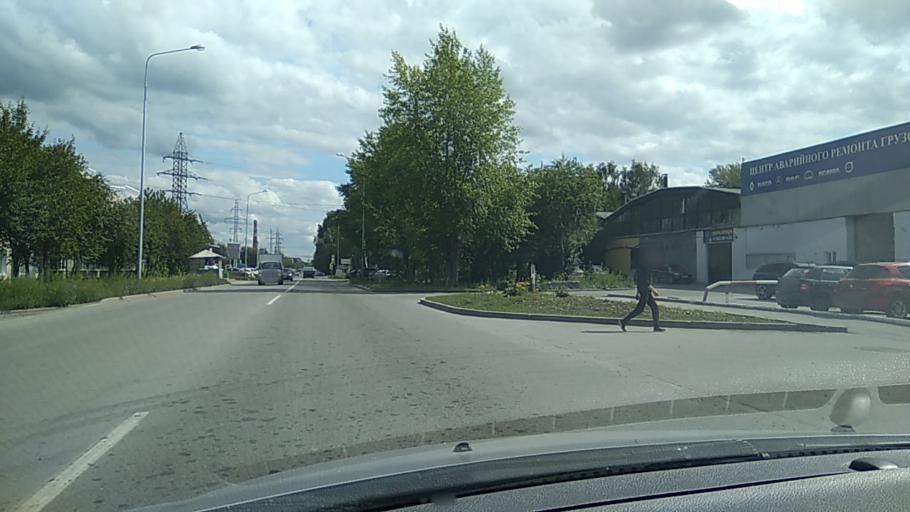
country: RU
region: Sverdlovsk
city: Shuvakish
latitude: 56.8858
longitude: 60.5304
